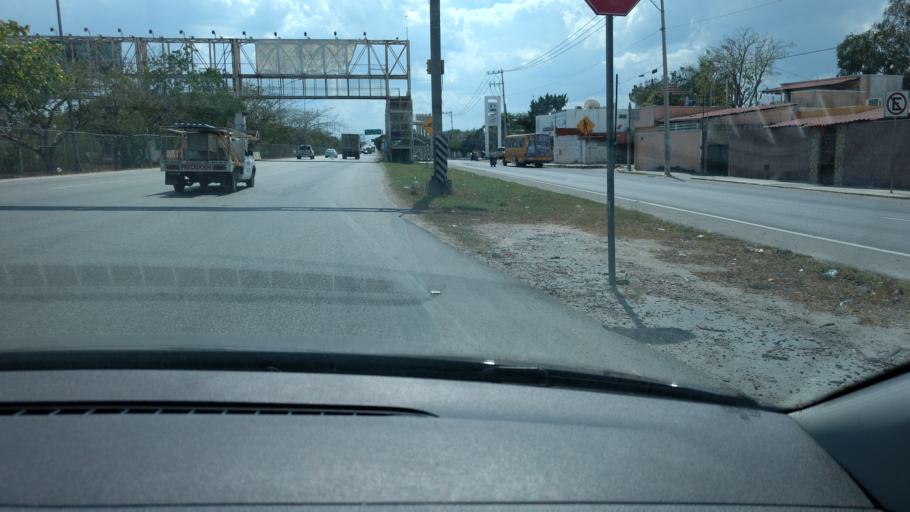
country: MX
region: Yucatan
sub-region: Kanasin
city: Kanasin
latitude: 20.9752
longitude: -89.5650
